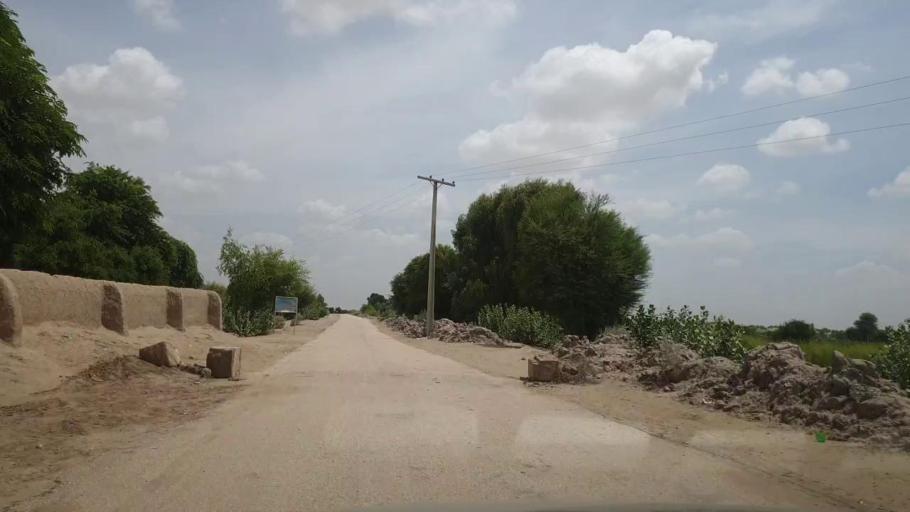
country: PK
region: Sindh
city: Kot Diji
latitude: 27.2071
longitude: 69.1173
